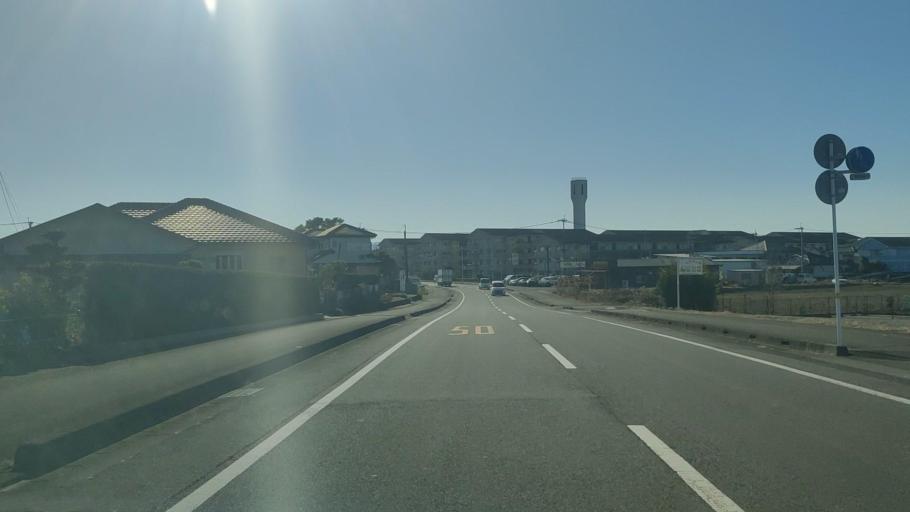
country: JP
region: Miyazaki
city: Miyazaki-shi
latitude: 31.9542
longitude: 131.4618
